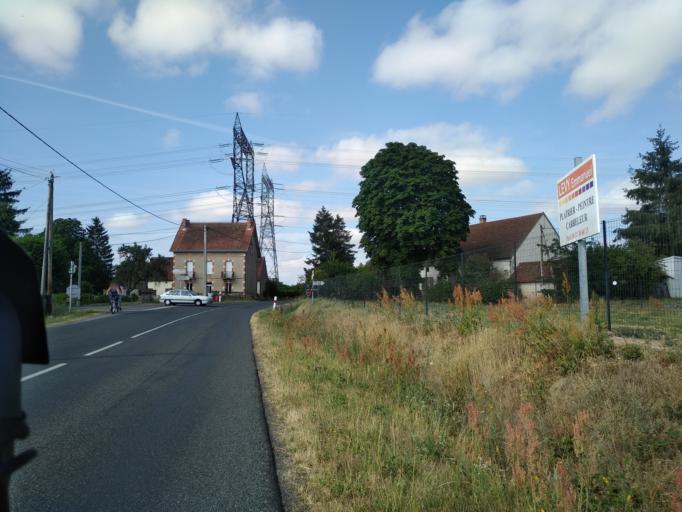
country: FR
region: Auvergne
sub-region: Departement de l'Allier
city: Saint-Pourcain-sur-Sioule
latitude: 46.2951
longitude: 3.2709
